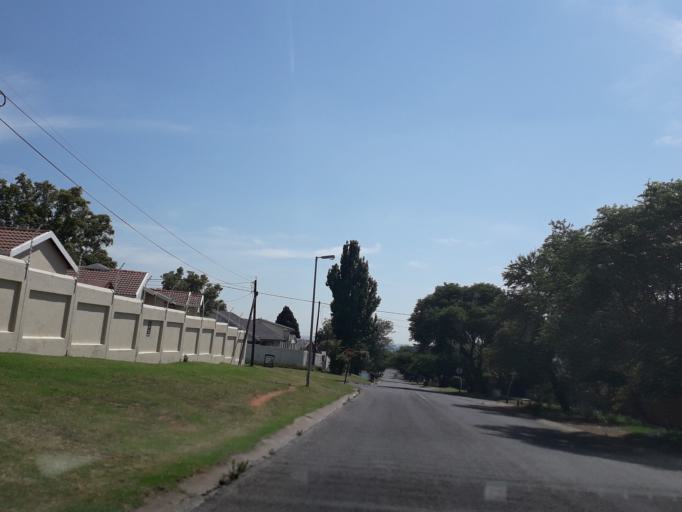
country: ZA
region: Gauteng
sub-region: City of Johannesburg Metropolitan Municipality
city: Johannesburg
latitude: -26.1105
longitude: 28.0072
